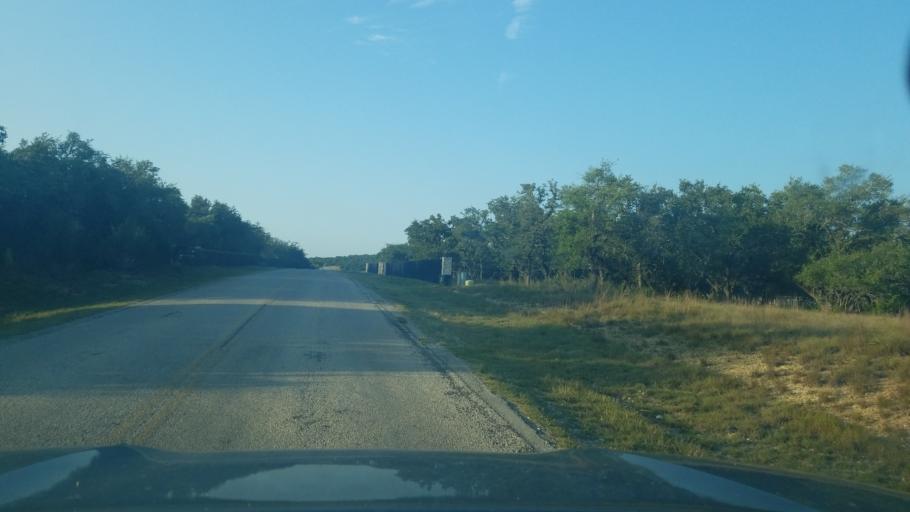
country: US
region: Texas
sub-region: Comal County
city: Bulverde
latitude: 29.8272
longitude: -98.4072
